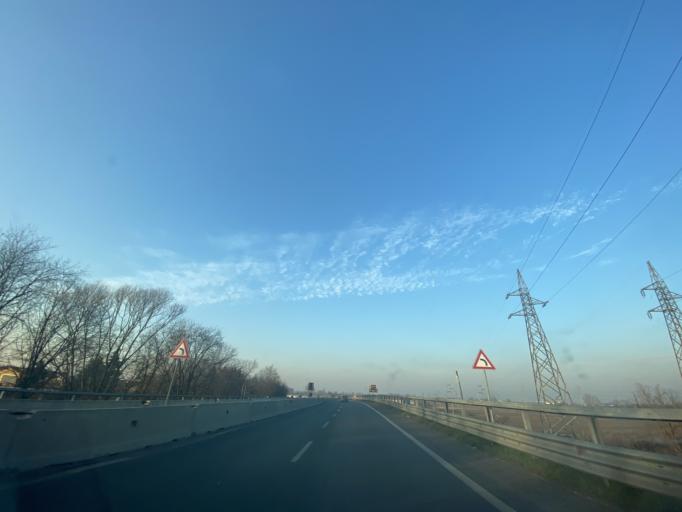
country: IT
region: Lombardy
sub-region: Citta metropolitana di Milano
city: Opera
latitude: 45.3763
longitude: 9.2271
